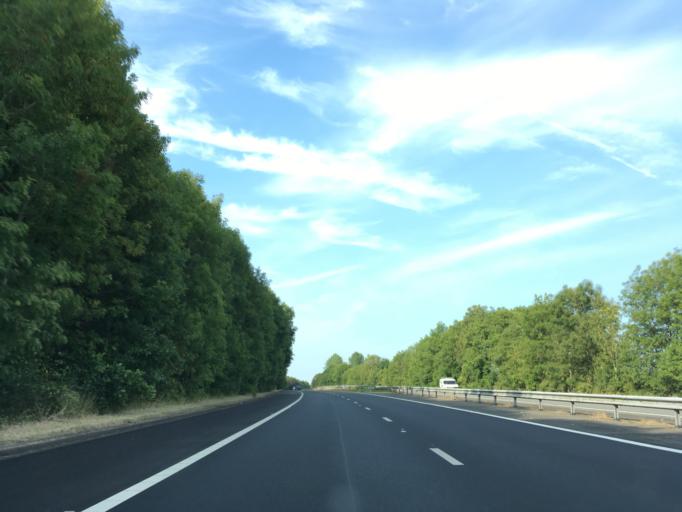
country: GB
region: Wales
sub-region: Monmouthshire
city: Caldicot
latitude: 51.6007
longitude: -2.7554
